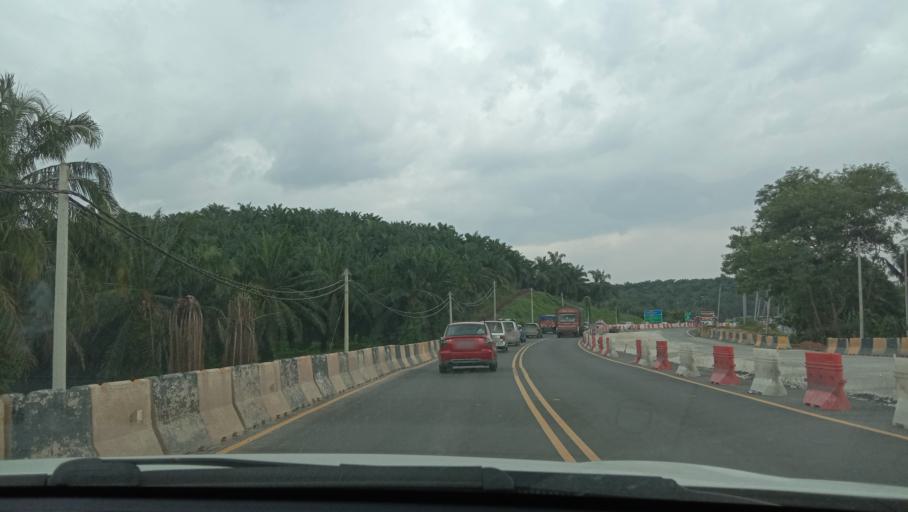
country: MY
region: Selangor
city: Batu Arang
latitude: 3.2623
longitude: 101.4618
